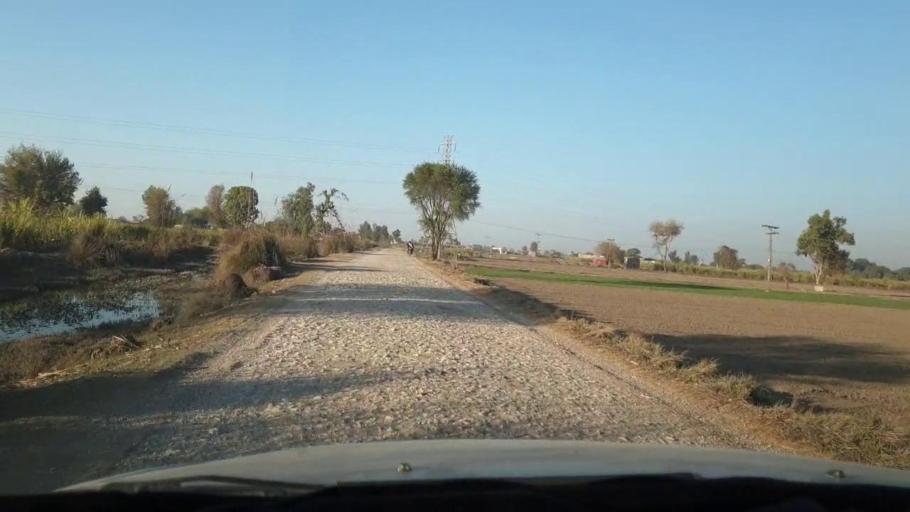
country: PK
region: Sindh
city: Ghotki
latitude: 27.9898
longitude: 69.2728
